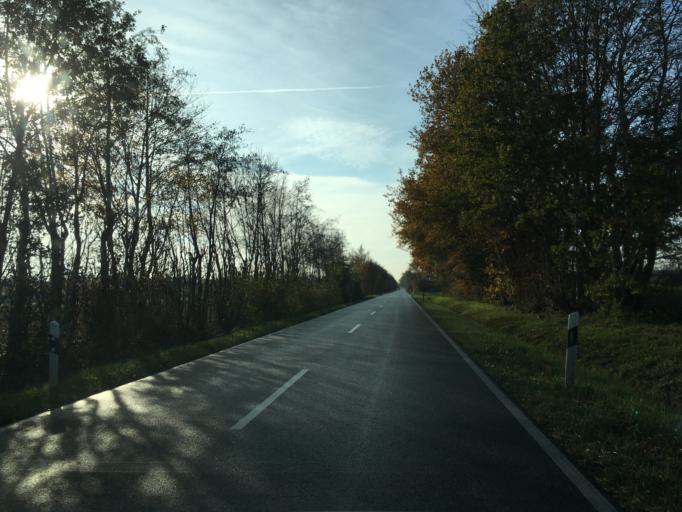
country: DE
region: North Rhine-Westphalia
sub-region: Regierungsbezirk Munster
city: Ahaus
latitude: 52.0414
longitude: 6.9689
